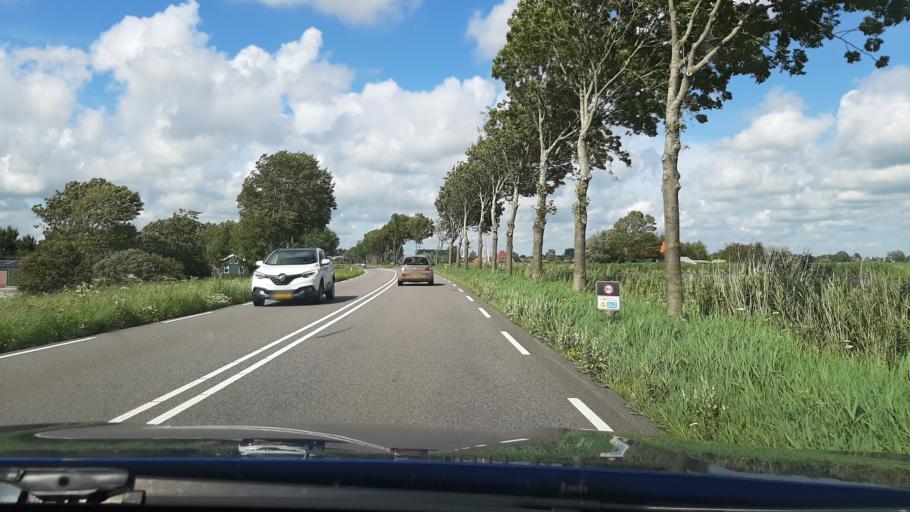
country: NL
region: North Holland
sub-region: Gemeente Zaanstad
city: Zaanstad
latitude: 52.4539
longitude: 4.7590
